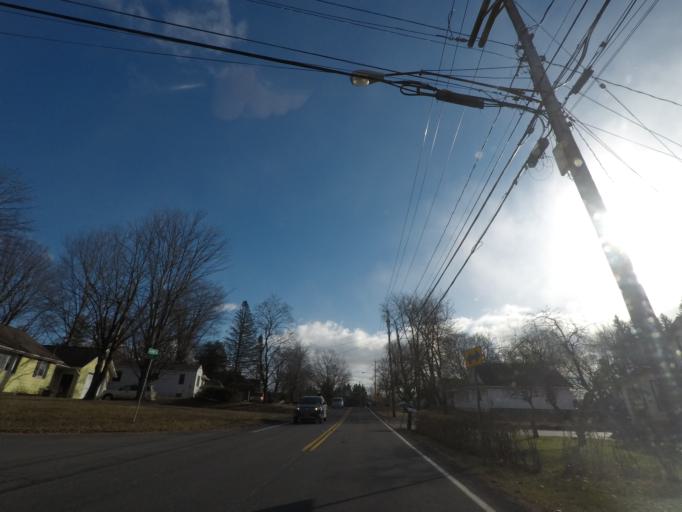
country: US
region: New York
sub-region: Schenectady County
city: Niskayuna
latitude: 42.7480
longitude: -73.8721
